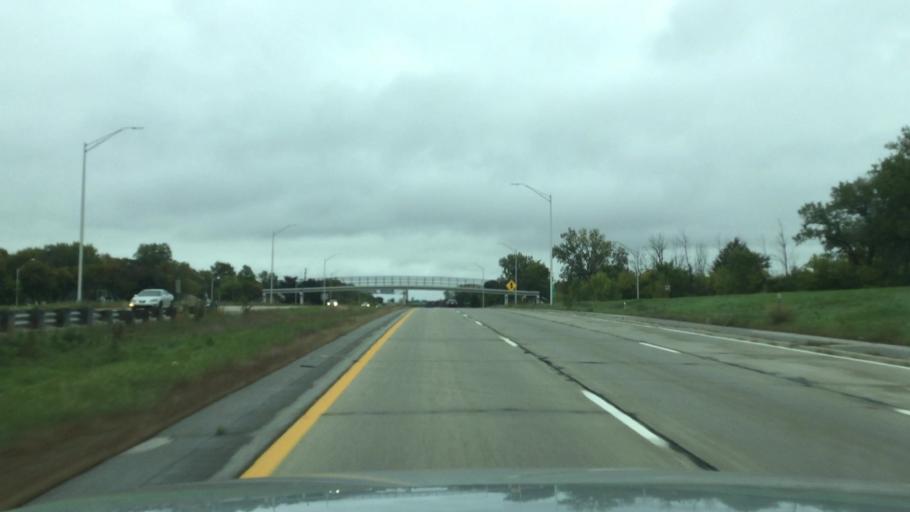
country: US
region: Michigan
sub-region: Saginaw County
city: Buena Vista
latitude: 43.4339
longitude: -83.9118
